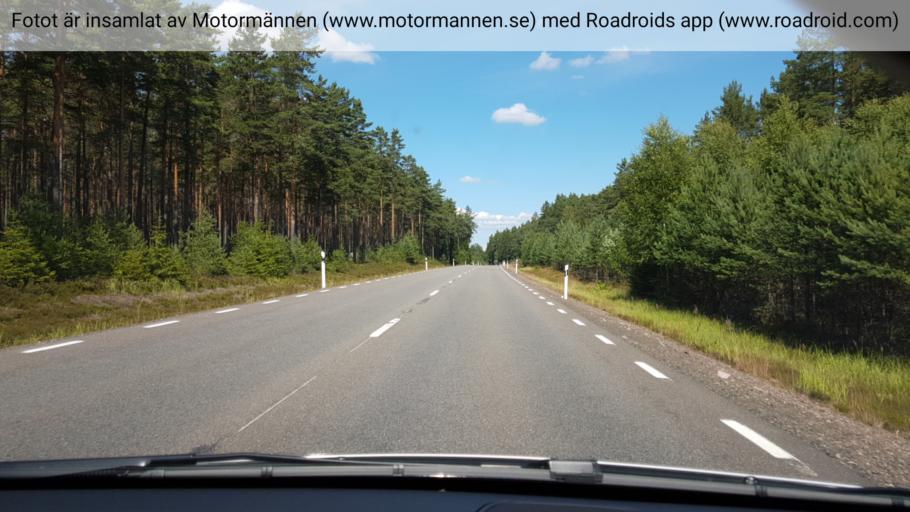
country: SE
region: Vaestra Goetaland
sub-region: Tibro Kommun
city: Tibro
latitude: 58.5360
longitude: 14.1510
